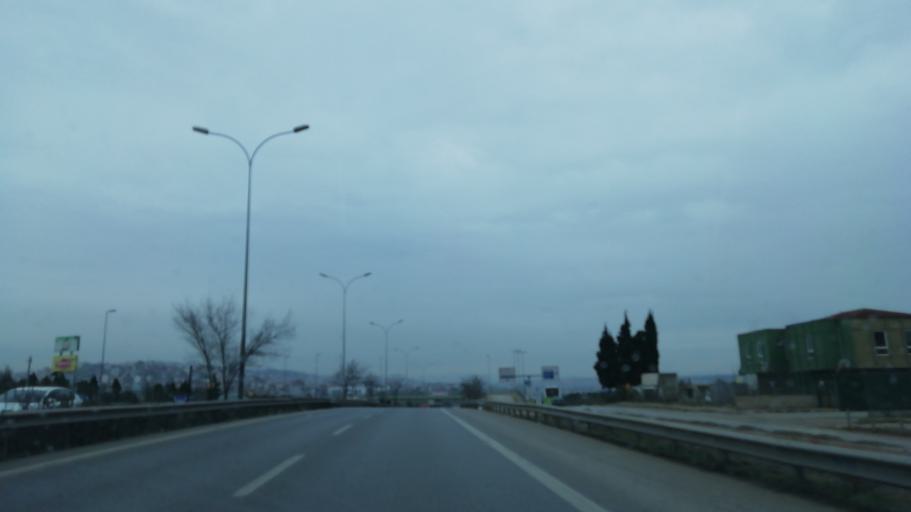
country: TR
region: Istanbul
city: Icmeler
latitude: 40.8224
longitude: 29.3543
